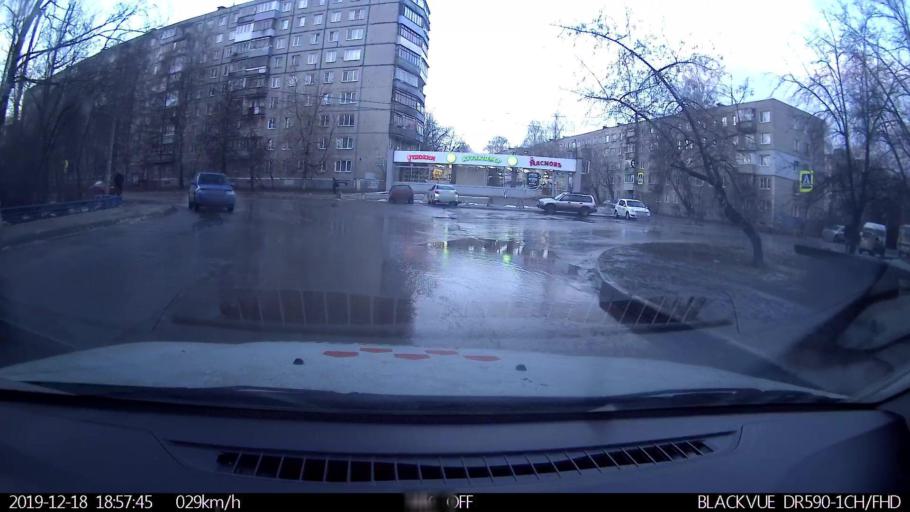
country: RU
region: Nizjnij Novgorod
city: Gorbatovka
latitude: 56.3371
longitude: 43.8401
